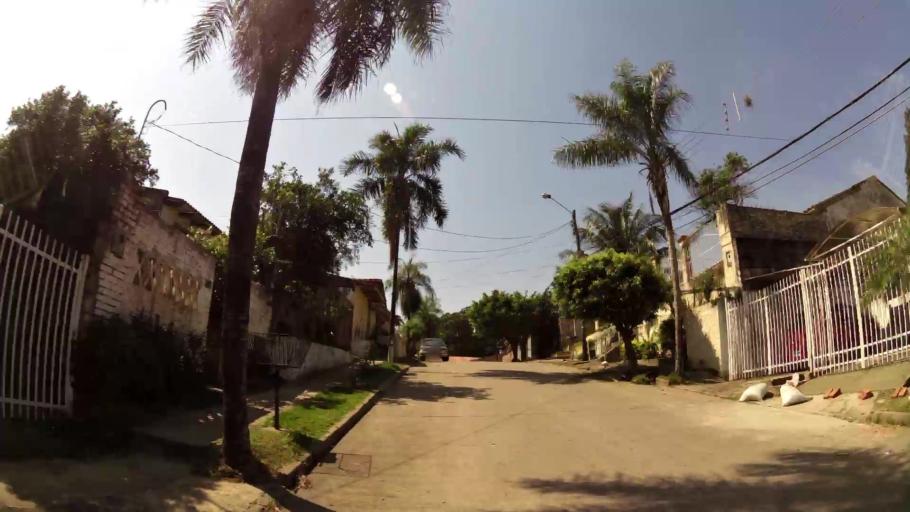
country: BO
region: Santa Cruz
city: Santa Cruz de la Sierra
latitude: -17.7421
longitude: -63.1783
